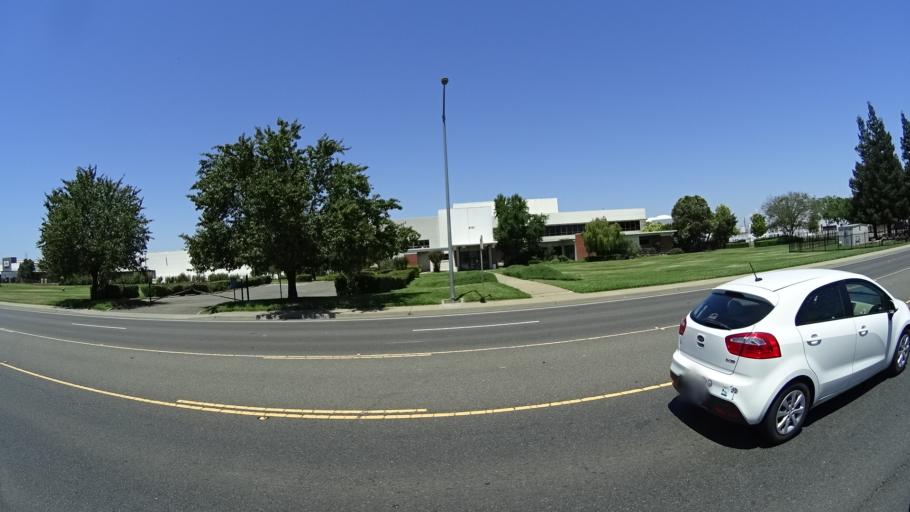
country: US
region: California
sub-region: Sacramento County
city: Florin
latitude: 38.5258
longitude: -121.4044
